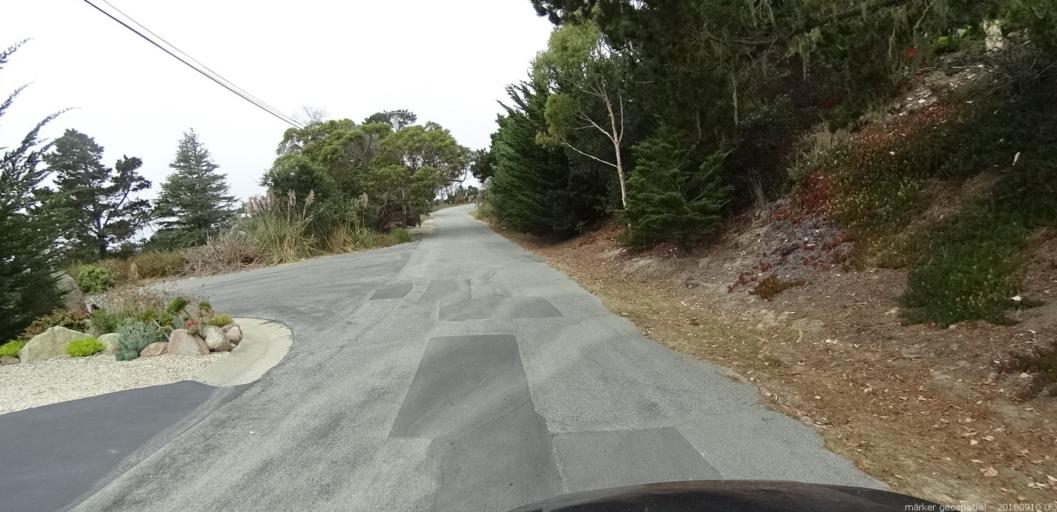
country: US
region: California
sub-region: Monterey County
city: Carmel-by-the-Sea
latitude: 36.4877
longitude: -121.9358
